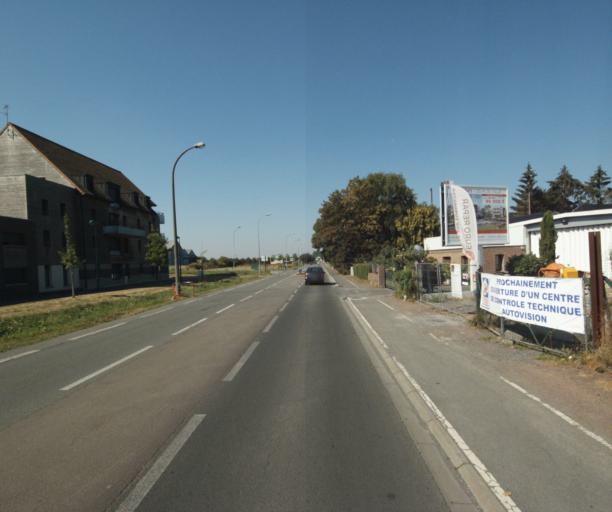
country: FR
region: Nord-Pas-de-Calais
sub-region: Departement du Nord
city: Wervicq-Sud
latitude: 50.7699
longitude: 3.0402
